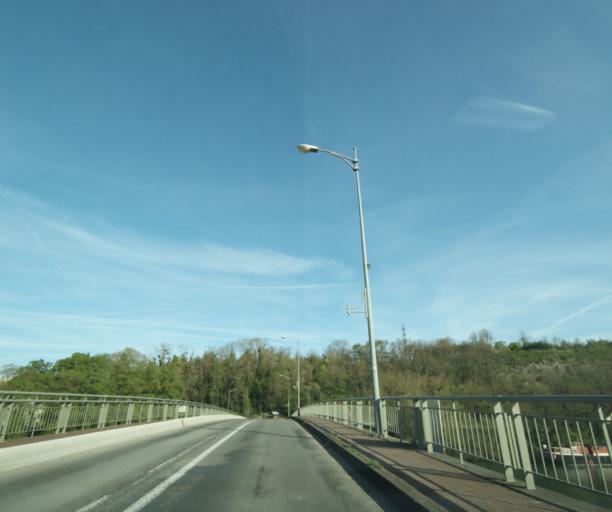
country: FR
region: Ile-de-France
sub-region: Departement de Seine-et-Marne
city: Saint-Mammes
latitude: 48.3897
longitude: 2.8075
